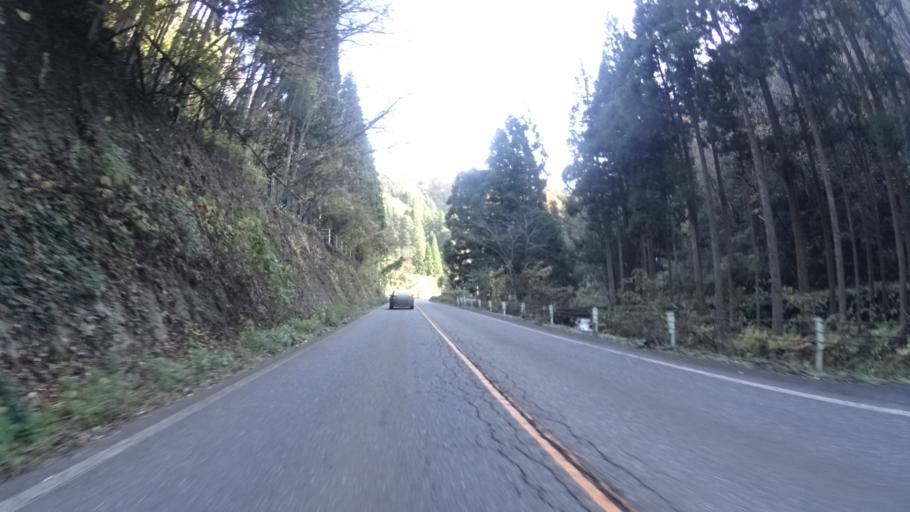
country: JP
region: Ishikawa
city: Tsurugi-asahimachi
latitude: 36.3731
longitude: 136.5743
